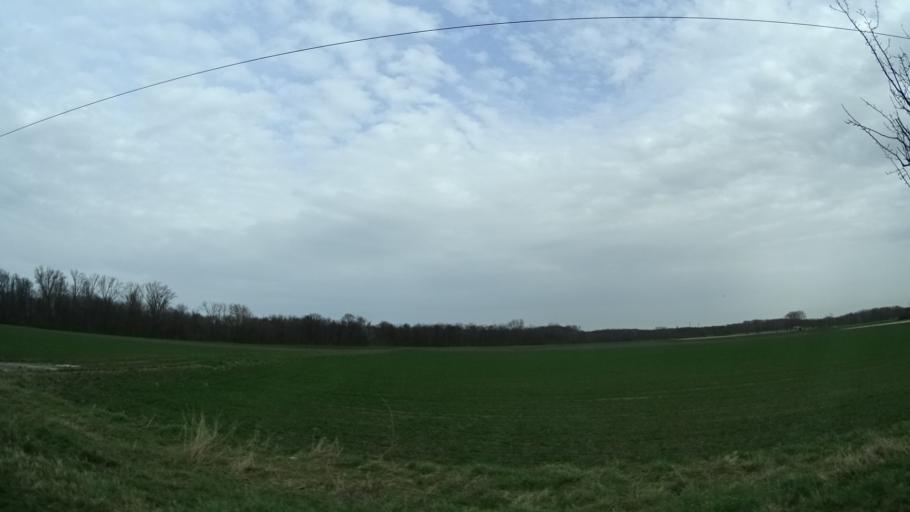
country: DE
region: Rheinland-Pfalz
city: Osthofen
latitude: 49.6930
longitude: 8.3689
